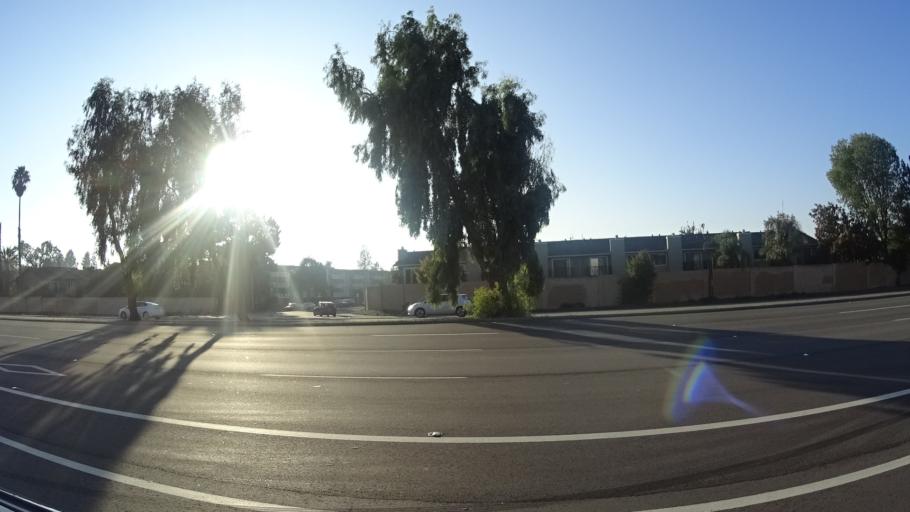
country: US
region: California
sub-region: Santa Clara County
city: Santa Clara
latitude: 37.3491
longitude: -121.9958
